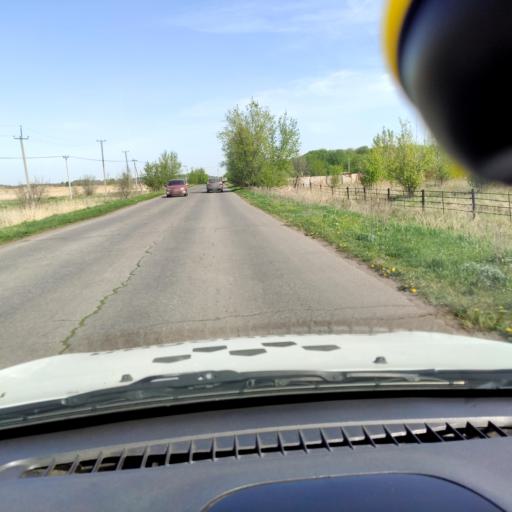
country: RU
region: Samara
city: Tol'yatti
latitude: 53.6463
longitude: 49.3189
